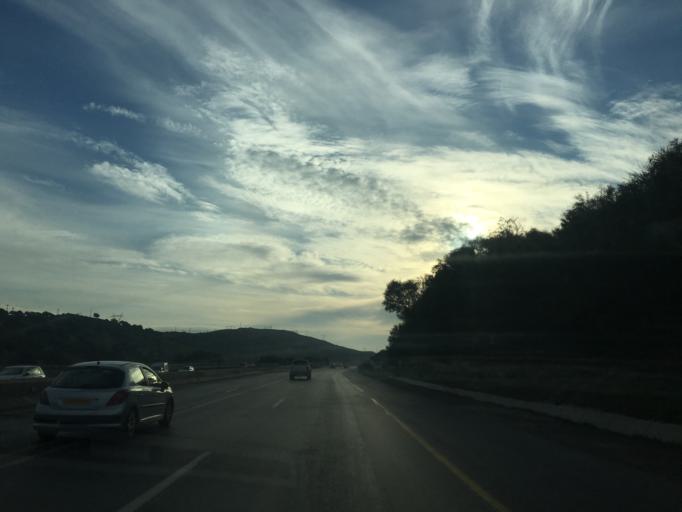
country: DZ
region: Bouira
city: Draa el Mizan
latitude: 36.4593
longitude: 3.7740
